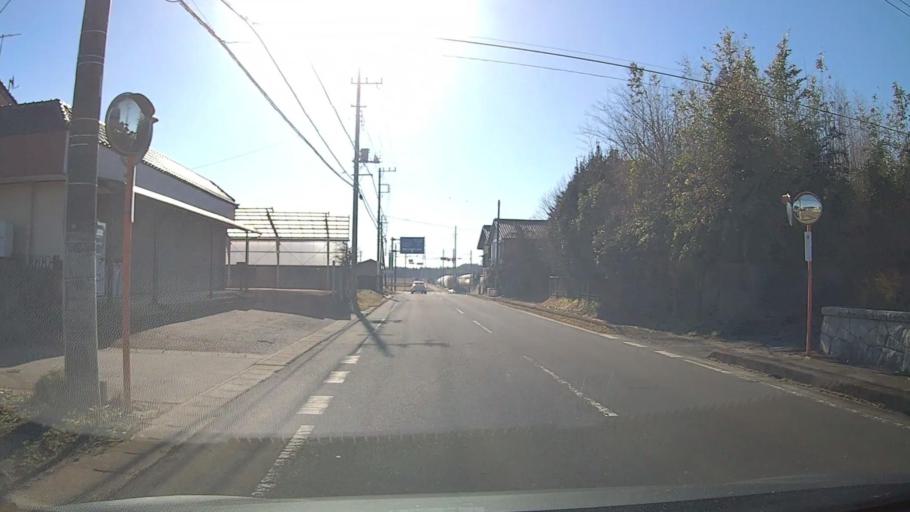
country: JP
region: Ibaraki
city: Mito-shi
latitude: 36.4221
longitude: 140.4462
